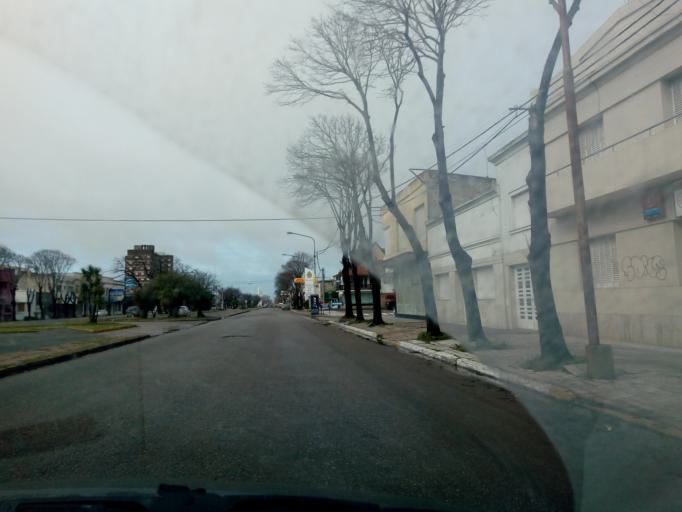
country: AR
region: Buenos Aires
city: Necochea
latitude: -38.5581
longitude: -58.7349
